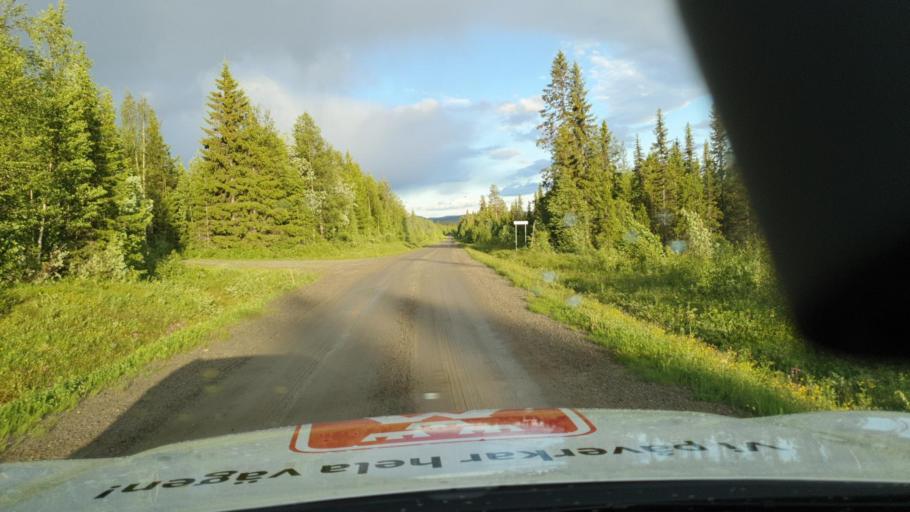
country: SE
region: Vaesterbotten
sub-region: Storumans Kommun
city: Storuman
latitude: 64.7600
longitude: 17.0704
